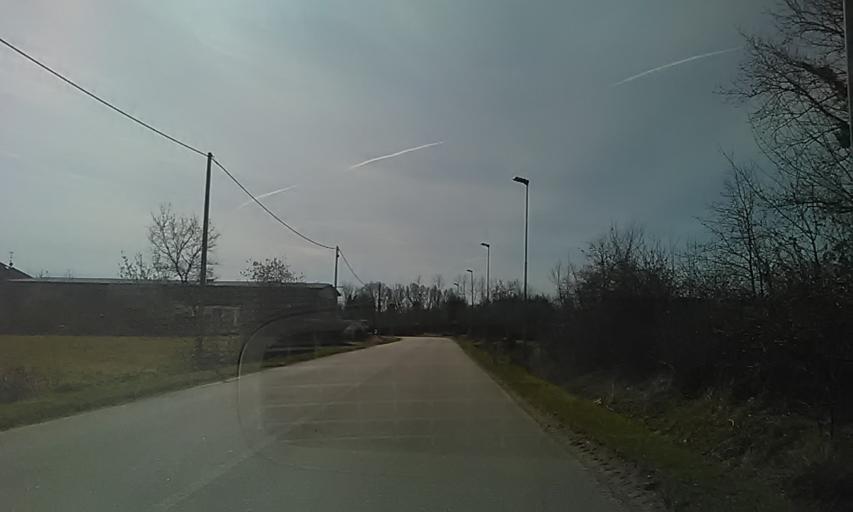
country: IT
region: Piedmont
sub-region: Provincia di Biella
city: Brusnengo
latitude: 45.5866
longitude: 8.2500
